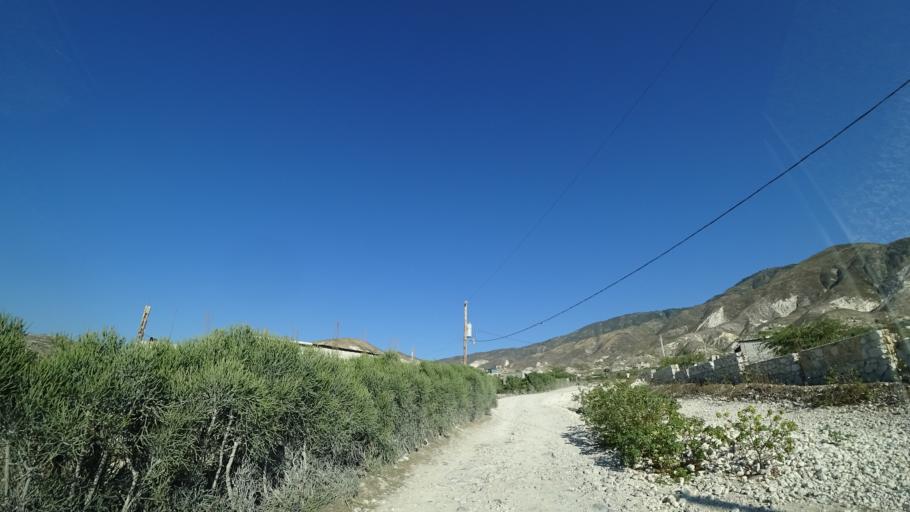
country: HT
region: Ouest
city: Croix des Bouquets
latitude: 18.6731
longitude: -72.2420
